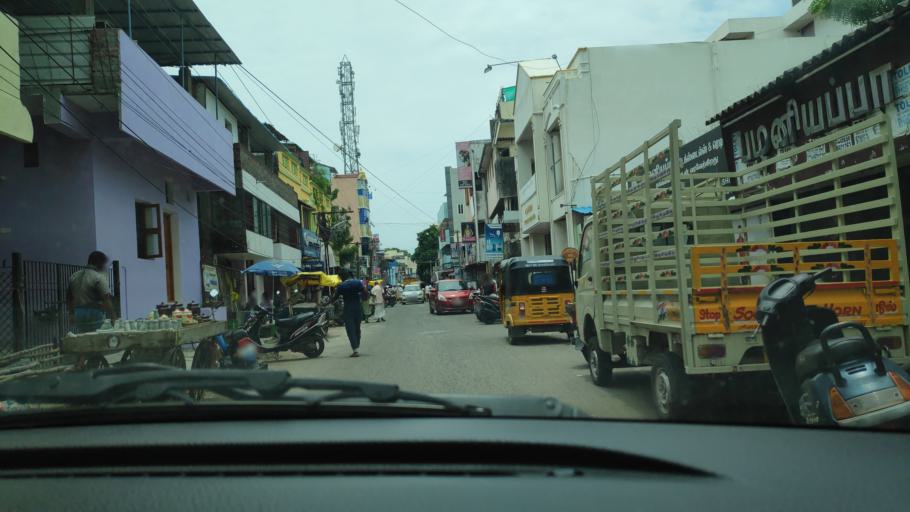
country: IN
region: Tamil Nadu
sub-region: Kancheepuram
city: Pallavaram
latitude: 12.9505
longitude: 80.1451
